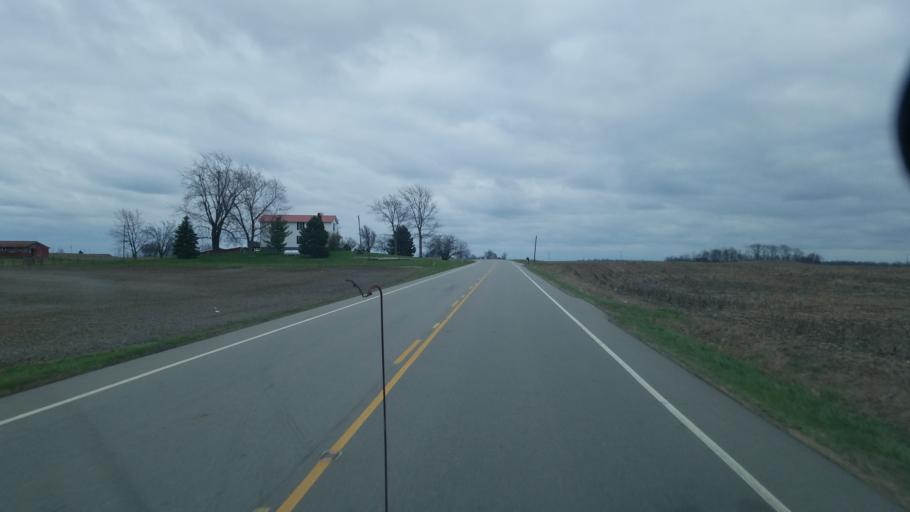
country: US
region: Ohio
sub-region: Fayette County
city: Washington Court House
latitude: 39.5740
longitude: -83.5127
